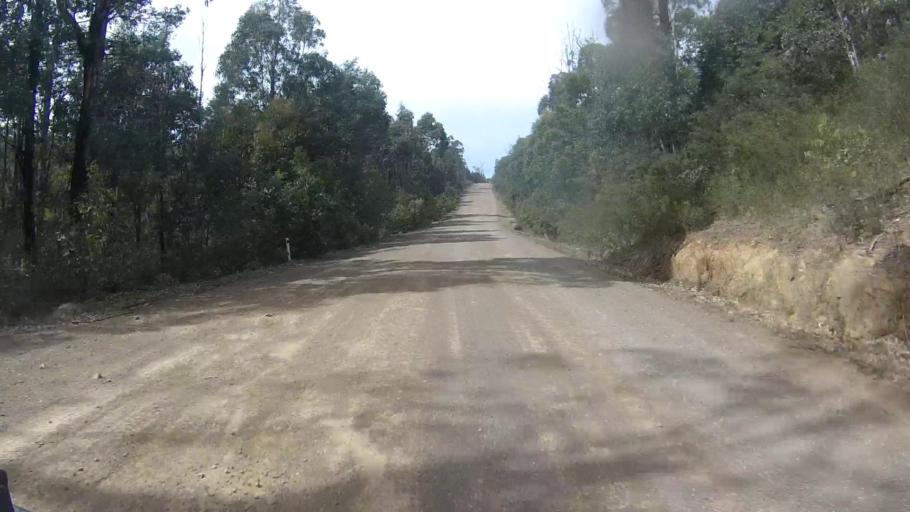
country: AU
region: Tasmania
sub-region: Sorell
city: Sorell
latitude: -42.7554
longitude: 147.8296
